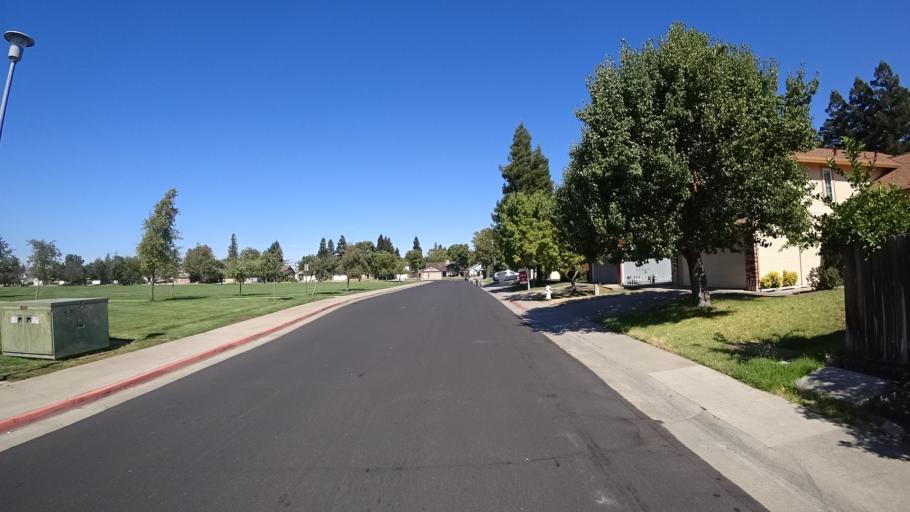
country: US
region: California
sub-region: Sacramento County
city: Laguna
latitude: 38.4306
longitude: -121.4340
